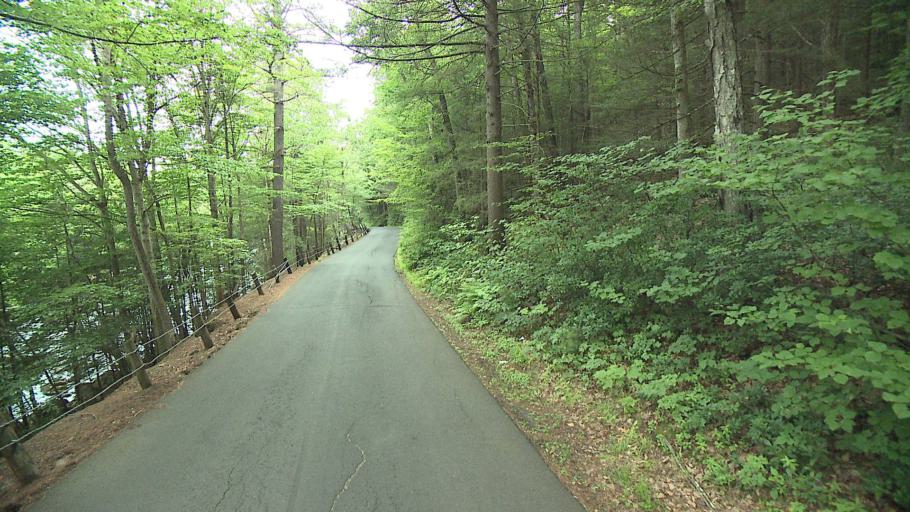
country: US
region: Connecticut
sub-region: Litchfield County
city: Winsted
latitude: 41.9506
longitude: -73.0130
